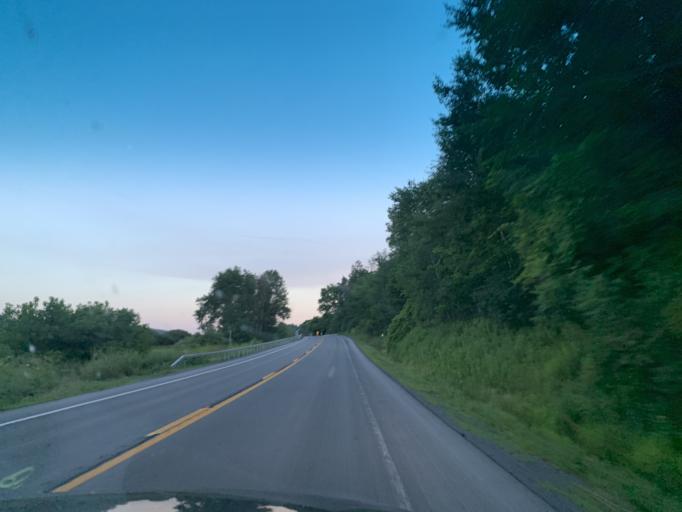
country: US
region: New York
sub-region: Chenango County
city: New Berlin
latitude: 42.7713
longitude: -75.2757
